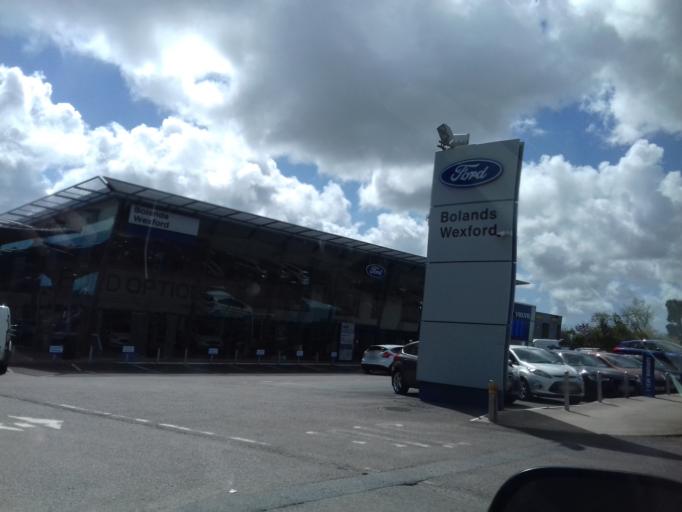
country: IE
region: Leinster
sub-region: Loch Garman
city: Loch Garman
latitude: 52.3520
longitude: -6.4546
